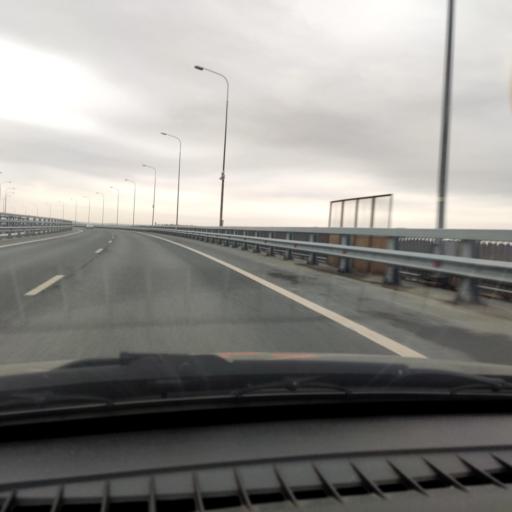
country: RU
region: Samara
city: Bereza
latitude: 53.5001
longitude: 50.1165
